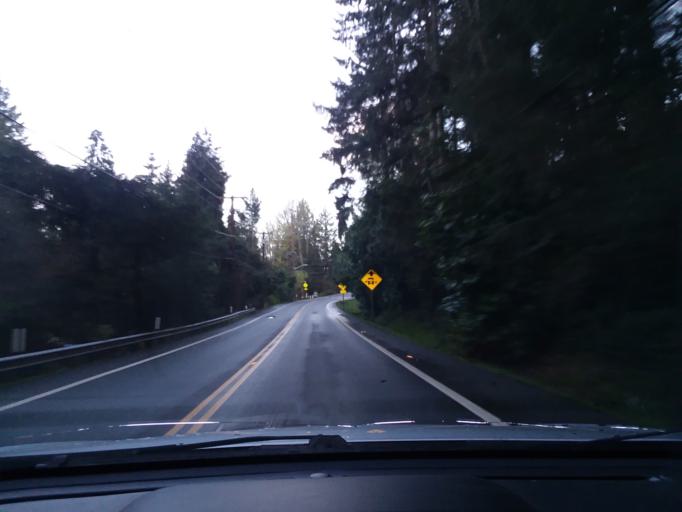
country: US
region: Washington
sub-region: King County
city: Kenmore
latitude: 47.7709
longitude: -122.2484
